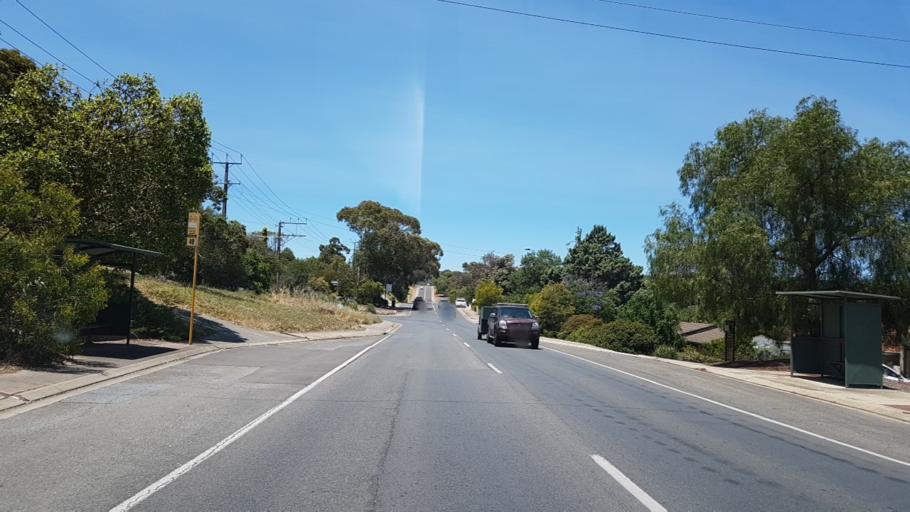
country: AU
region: South Australia
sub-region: Marion
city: Trott Park
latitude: -35.0830
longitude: 138.5514
